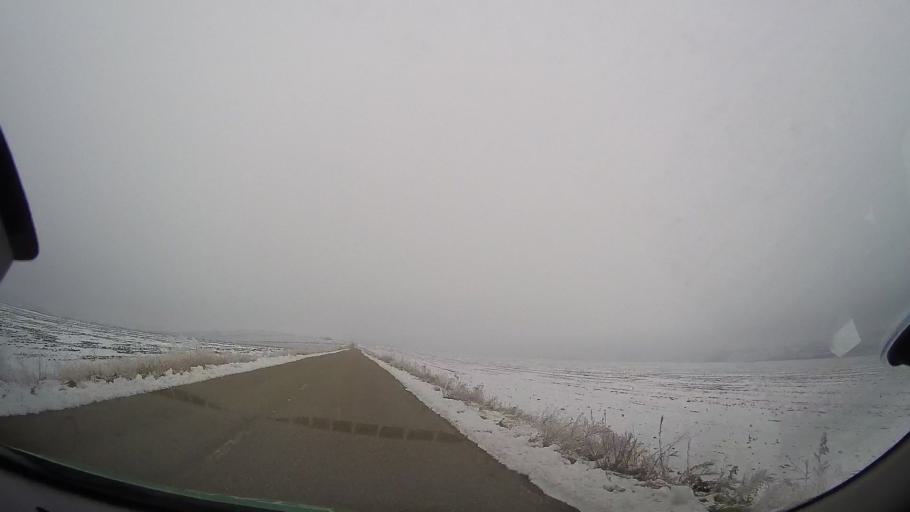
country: RO
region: Vaslui
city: Coroiesti
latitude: 46.2221
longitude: 27.4788
